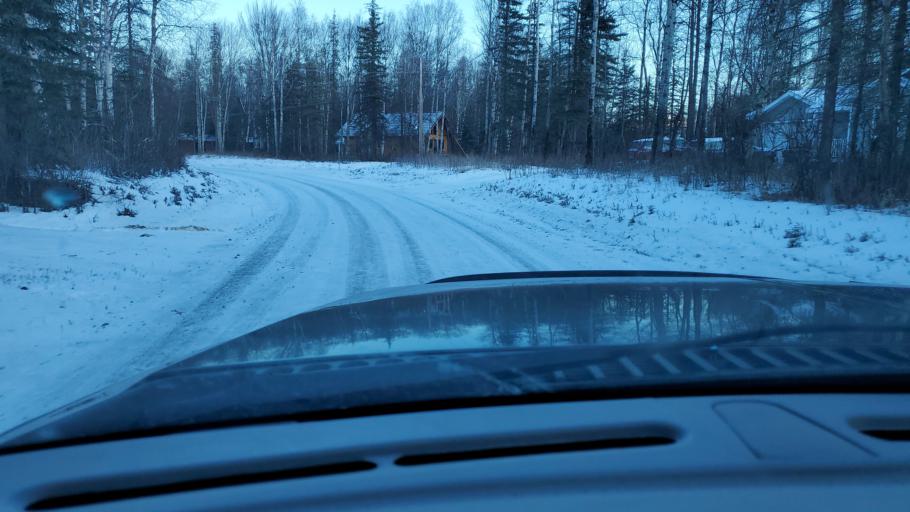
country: US
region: Alaska
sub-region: Matanuska-Susitna Borough
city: Lakes
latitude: 61.6653
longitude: -149.2958
